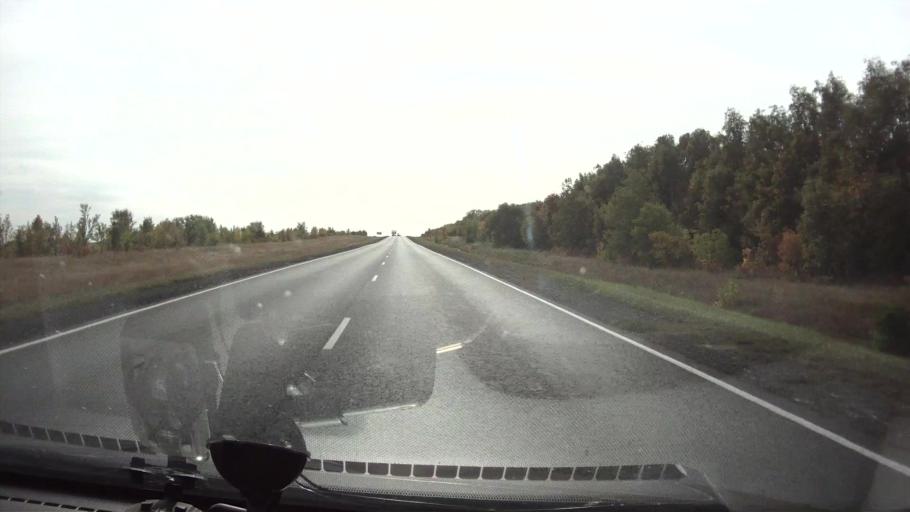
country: RU
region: Saratov
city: Balakovo
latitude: 52.1869
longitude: 47.8487
